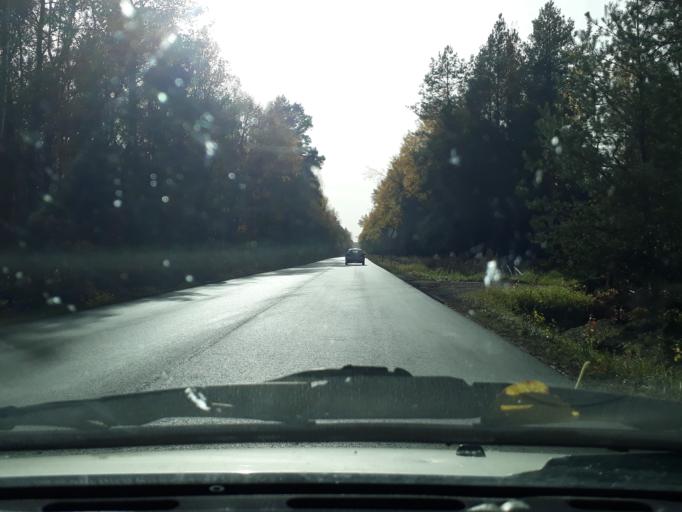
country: PL
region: Silesian Voivodeship
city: Miasteczko Slaskie
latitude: 50.5173
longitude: 18.9517
